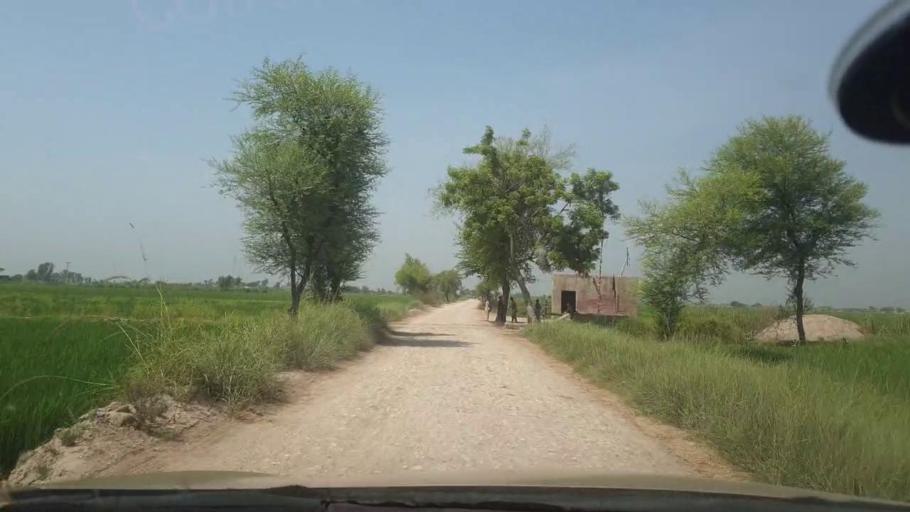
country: PK
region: Sindh
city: Shahdadkot
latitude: 27.7569
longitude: 67.9452
